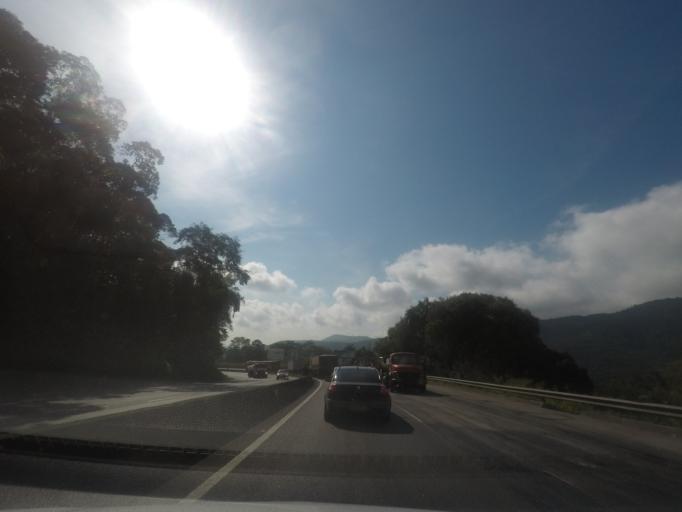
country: BR
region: Parana
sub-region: Antonina
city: Antonina
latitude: -25.5681
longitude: -48.8121
